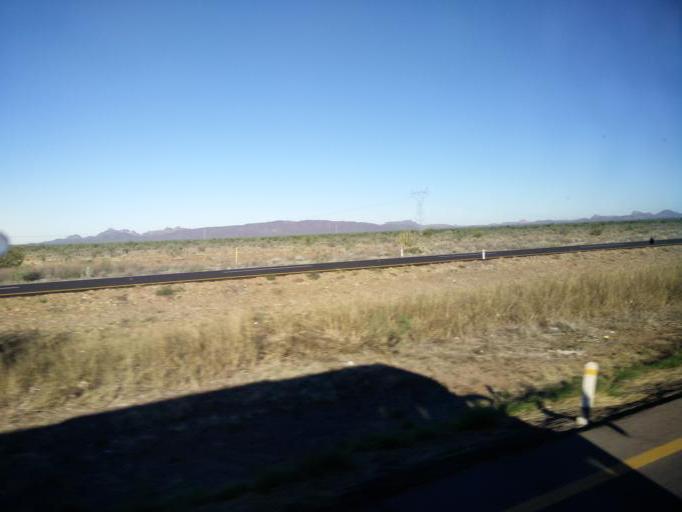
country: MX
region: Sonora
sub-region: Empalme
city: Empalme
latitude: 28.3067
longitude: -111.0416
